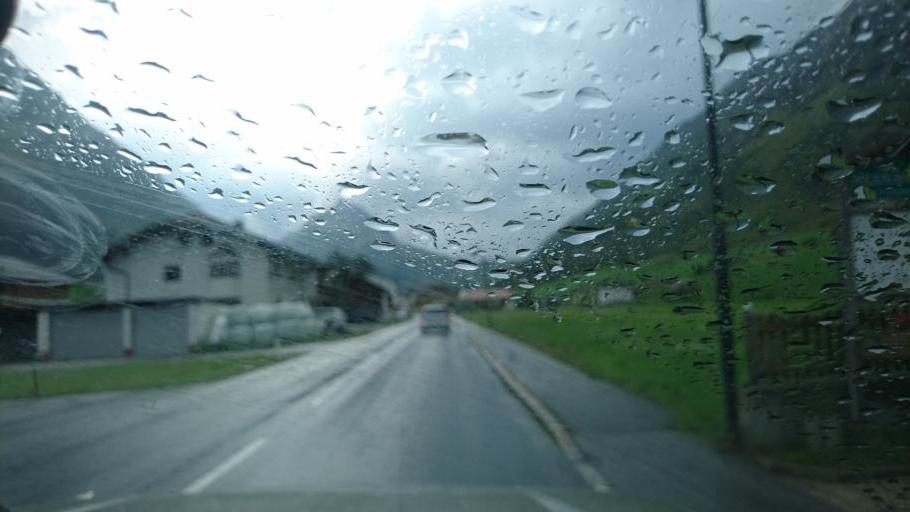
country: AT
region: Tyrol
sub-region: Politischer Bezirk Landeck
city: Galtur
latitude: 46.9709
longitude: 10.1945
